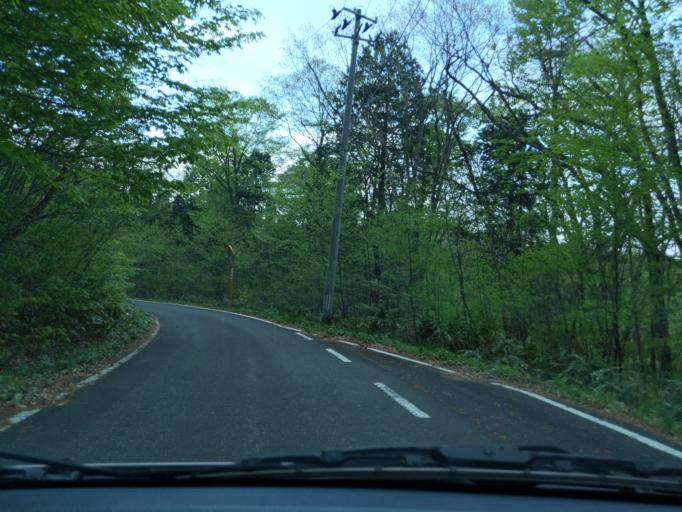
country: JP
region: Iwate
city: Ichinoseki
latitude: 38.9040
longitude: 140.8388
